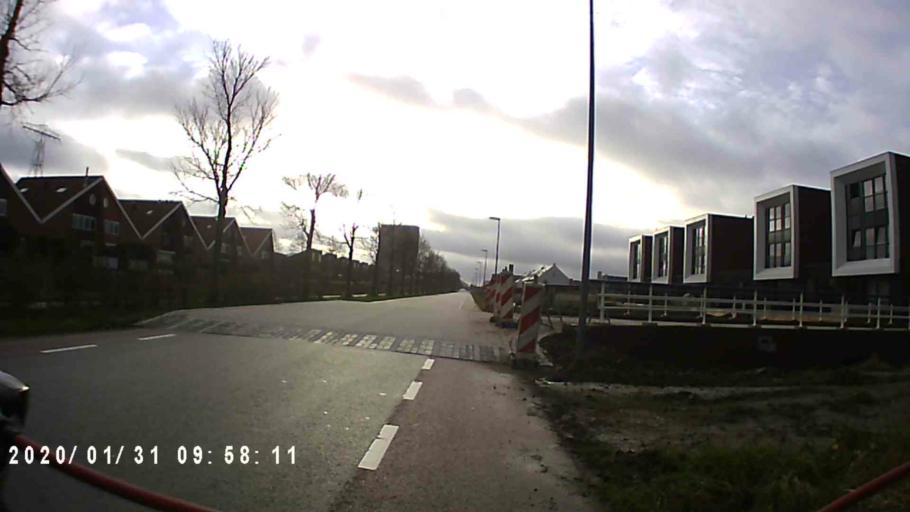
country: NL
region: Groningen
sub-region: Gemeente Groningen
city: Korrewegwijk
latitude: 53.2405
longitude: 6.5225
